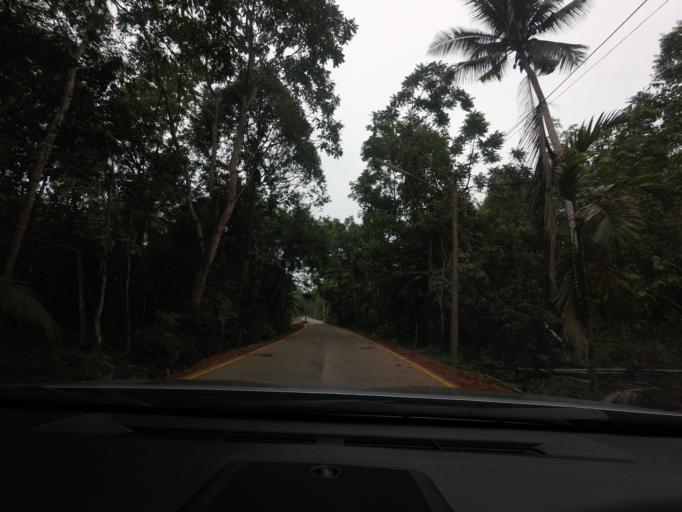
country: TH
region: Narathiwat
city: Rueso
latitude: 6.4100
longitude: 101.5274
